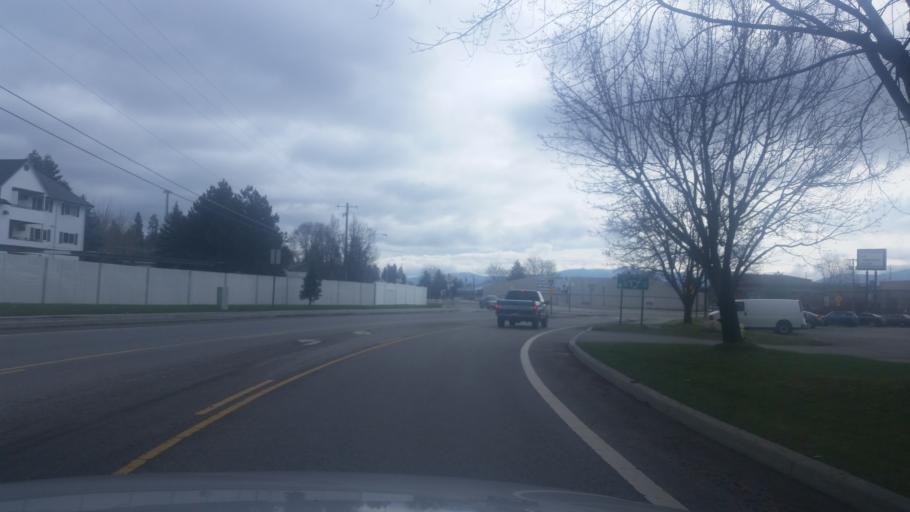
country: US
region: Washington
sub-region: Spokane County
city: Spokane Valley
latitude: 47.6777
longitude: -117.2493
